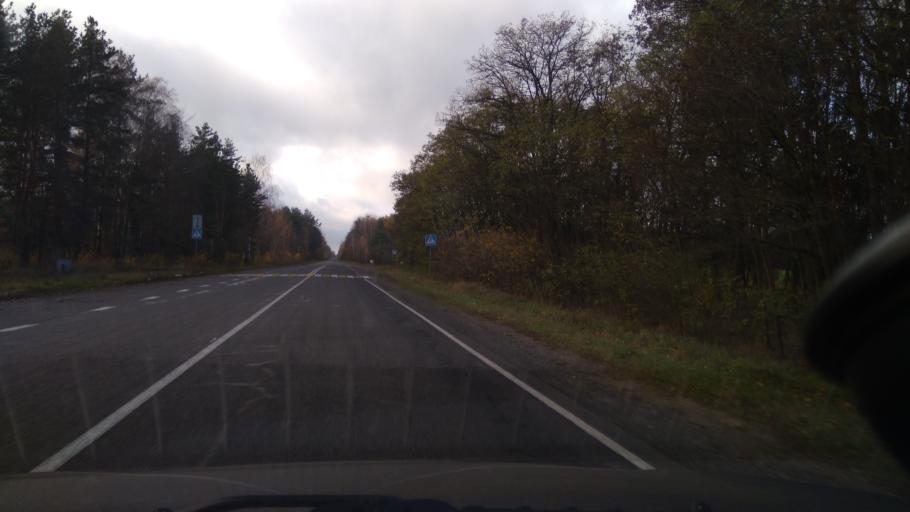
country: BY
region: Minsk
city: Urechcha
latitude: 53.2096
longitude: 27.9809
